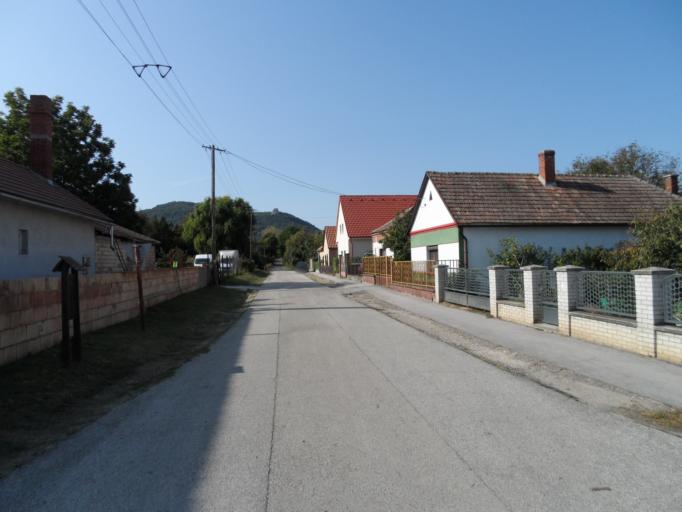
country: HU
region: Veszprem
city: Devecser
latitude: 47.1641
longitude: 17.3870
